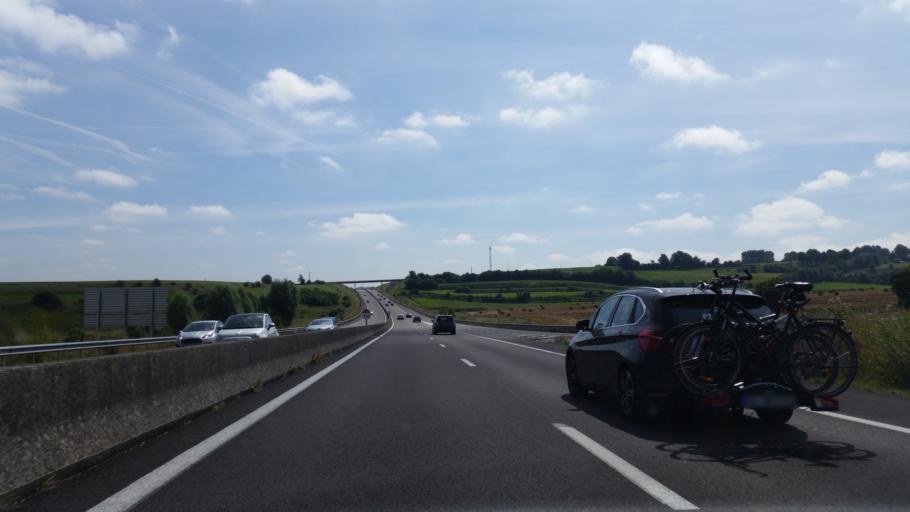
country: FR
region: Haute-Normandie
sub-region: Departement de la Seine-Maritime
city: Neufchatel-en-Bray
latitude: 49.7423
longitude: 1.5341
